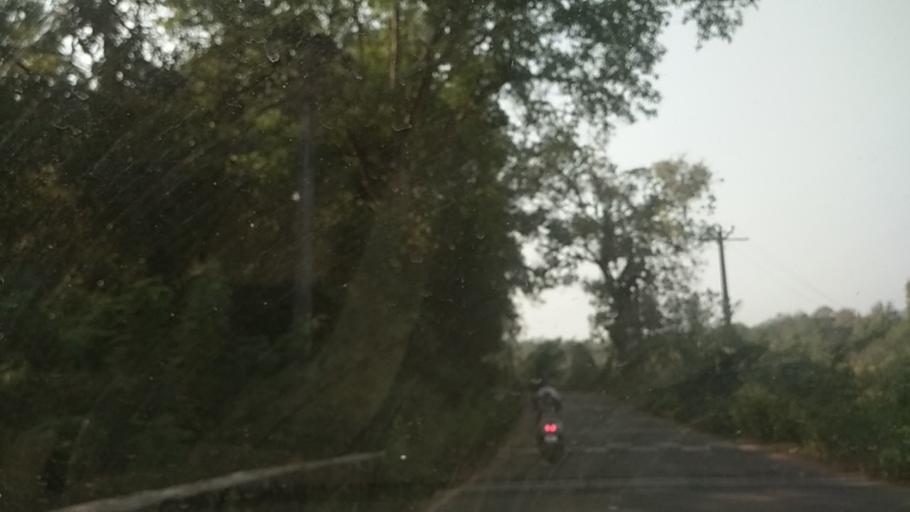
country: IN
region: Goa
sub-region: North Goa
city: Pernem
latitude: 15.7126
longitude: 73.8104
